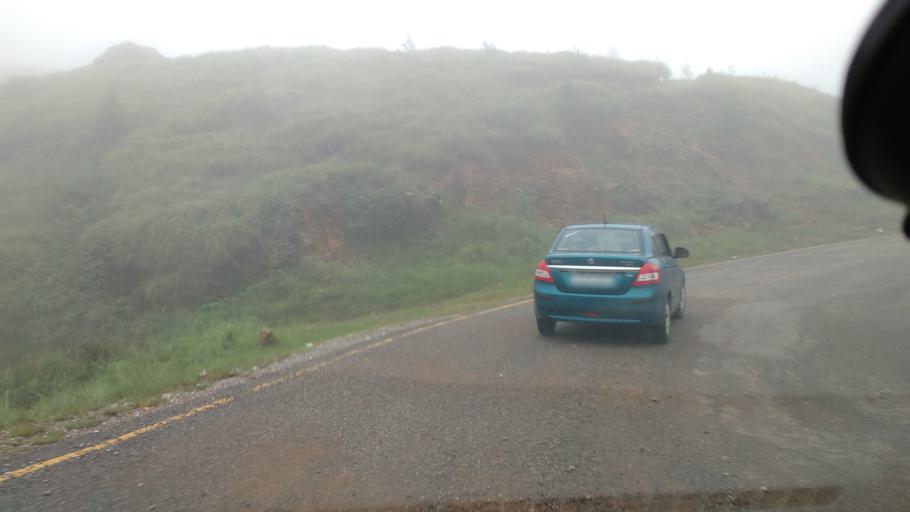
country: IN
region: Meghalaya
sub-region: East Khasi Hills
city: Cherrapunji
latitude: 25.2892
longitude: 91.7148
